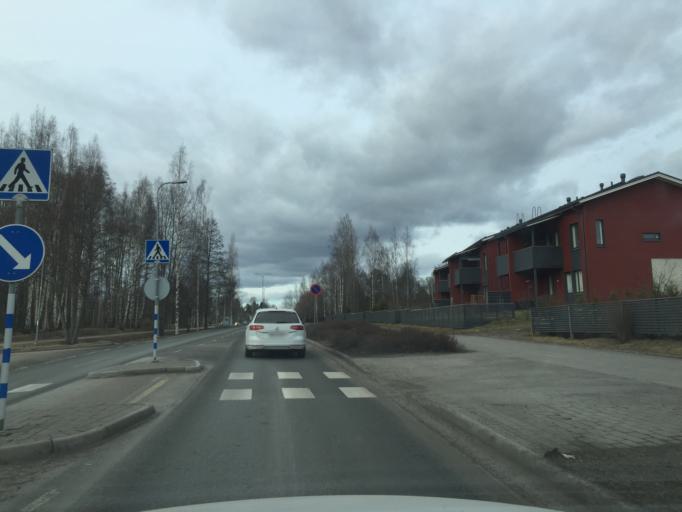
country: FI
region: Uusimaa
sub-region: Helsinki
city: Teekkarikylae
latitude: 60.2855
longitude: 24.8730
